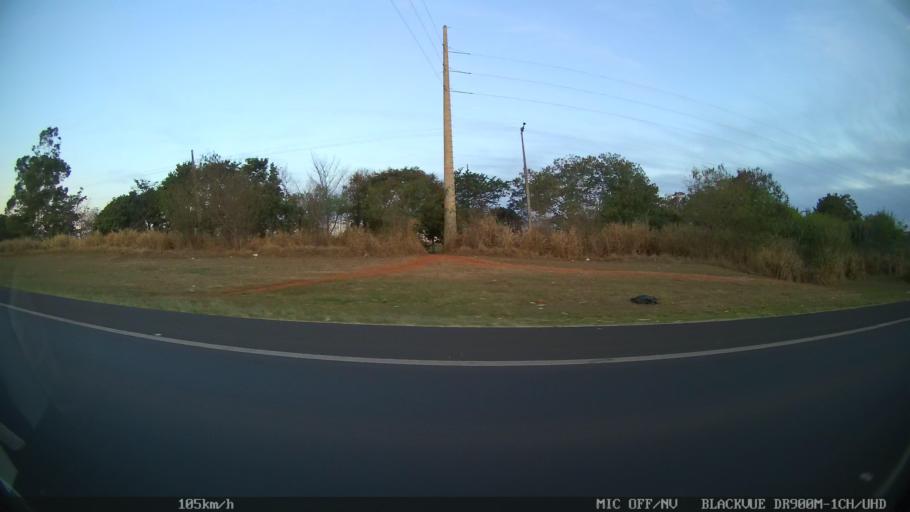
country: BR
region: Sao Paulo
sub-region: Catanduva
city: Catanduva
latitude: -21.1190
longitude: -48.9860
